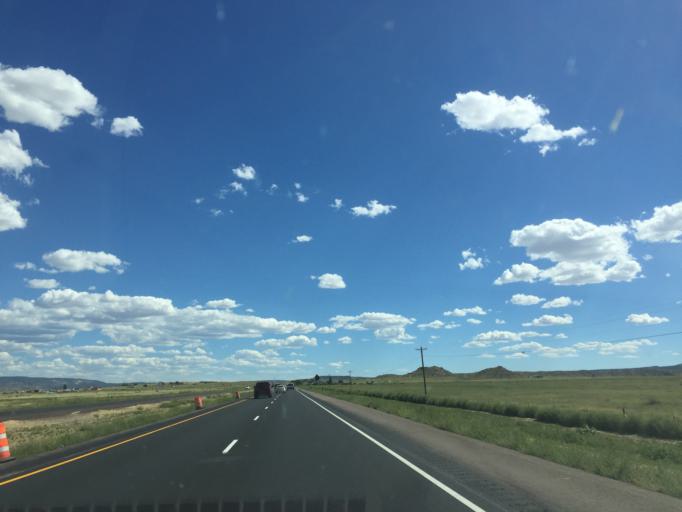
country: US
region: New Mexico
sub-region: McKinley County
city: Twin Lakes
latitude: 35.7498
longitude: -108.7754
